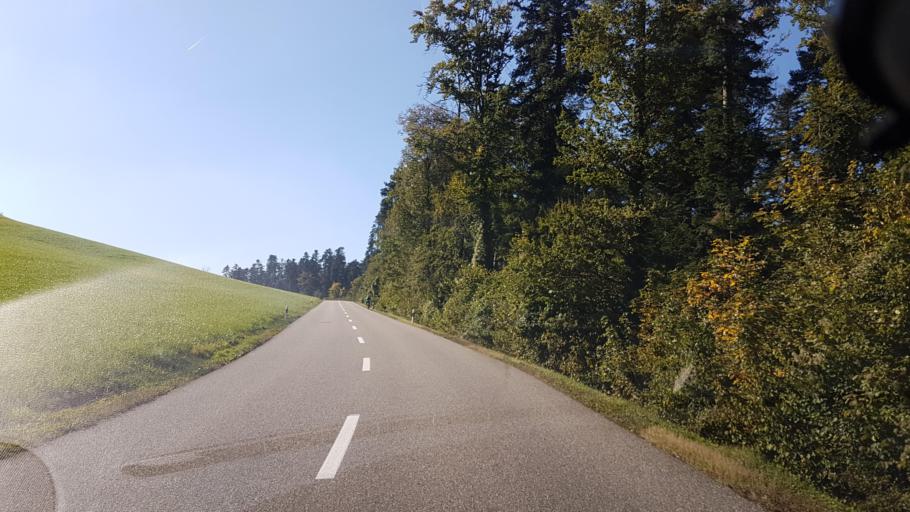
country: CH
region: Aargau
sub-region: Bezirk Laufenburg
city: Sulz
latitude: 47.5185
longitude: 8.1169
